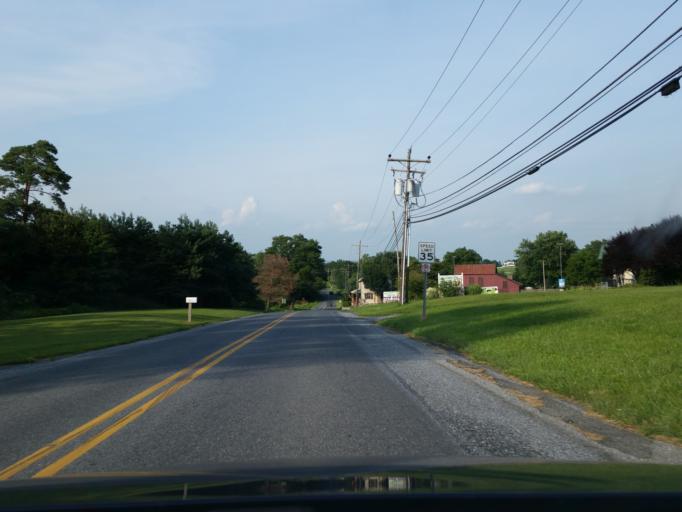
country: US
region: Pennsylvania
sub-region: Dauphin County
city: Palmdale
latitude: 40.3814
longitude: -76.6408
